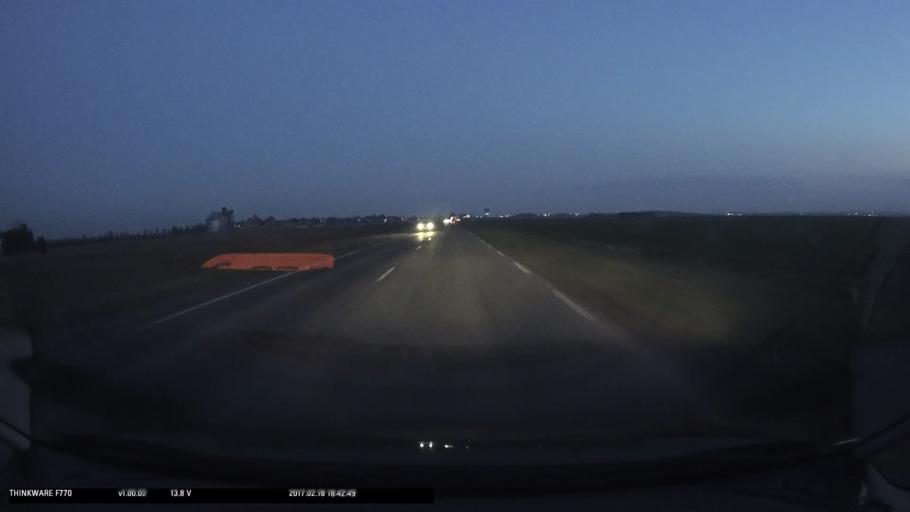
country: FR
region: Ile-de-France
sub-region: Departement du Val-d'Oise
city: Osny
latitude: 49.0964
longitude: 2.0489
